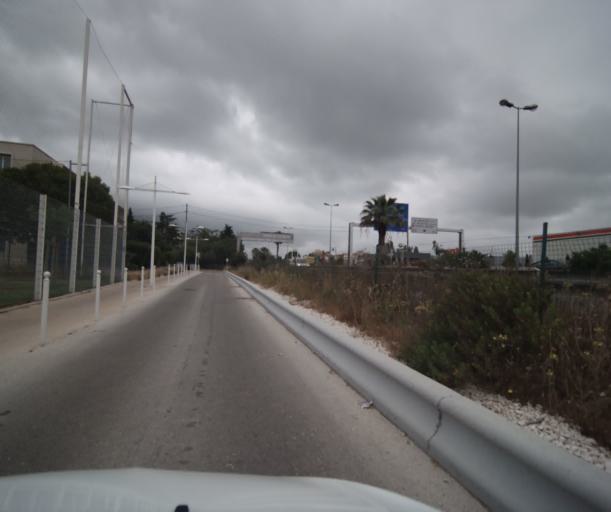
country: FR
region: Provence-Alpes-Cote d'Azur
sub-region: Departement du Var
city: La Valette-du-Var
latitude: 43.1278
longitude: 5.9751
